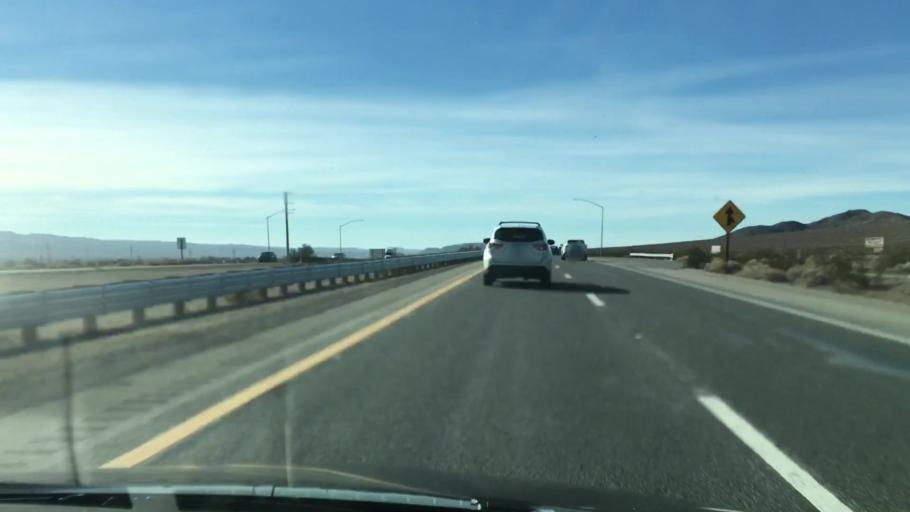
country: US
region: California
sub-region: San Bernardino County
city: Barstow
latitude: 34.9176
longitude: -116.7744
